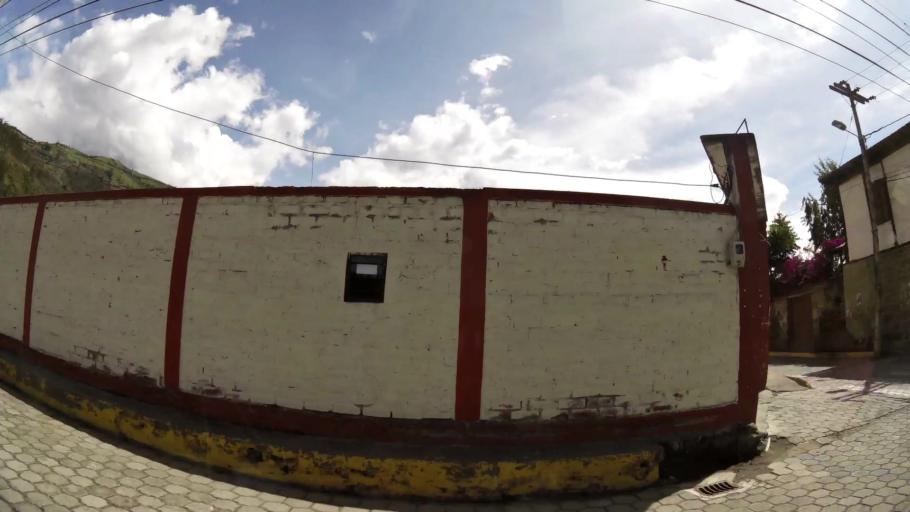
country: EC
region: Chimborazo
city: Guano
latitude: -1.5675
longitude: -78.5314
